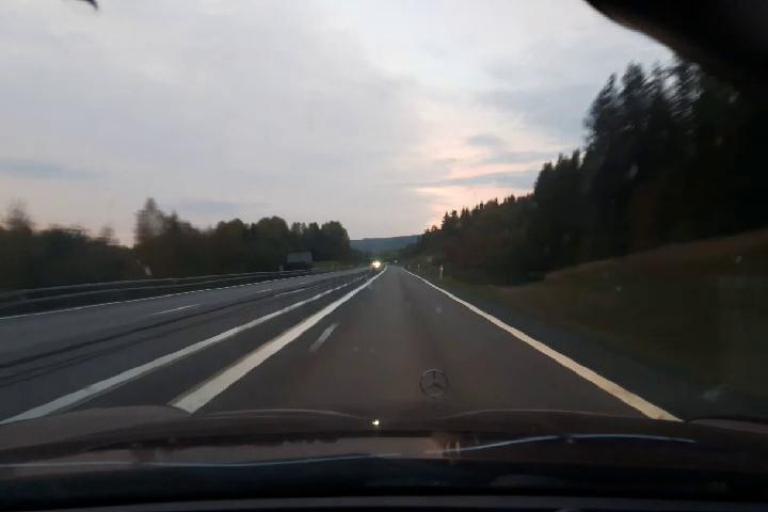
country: SE
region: Vaesternorrland
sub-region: Kramfors Kommun
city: Nordingra
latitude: 62.9334
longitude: 18.0953
